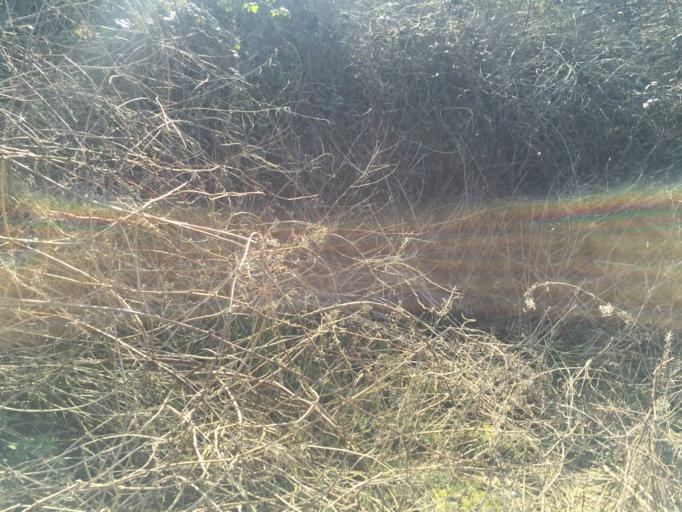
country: BE
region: Flanders
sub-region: Provincie Limburg
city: Sint-Pieters-Voeren
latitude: 50.7214
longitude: 5.7916
